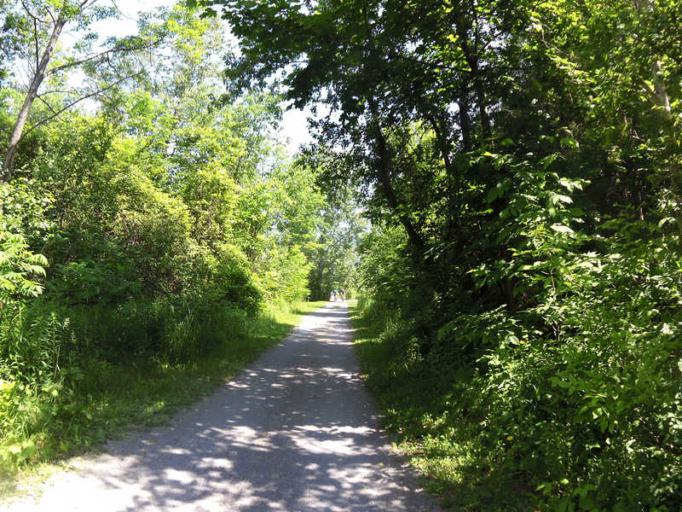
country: CA
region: Ontario
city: Peterborough
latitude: 44.3963
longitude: -78.2639
